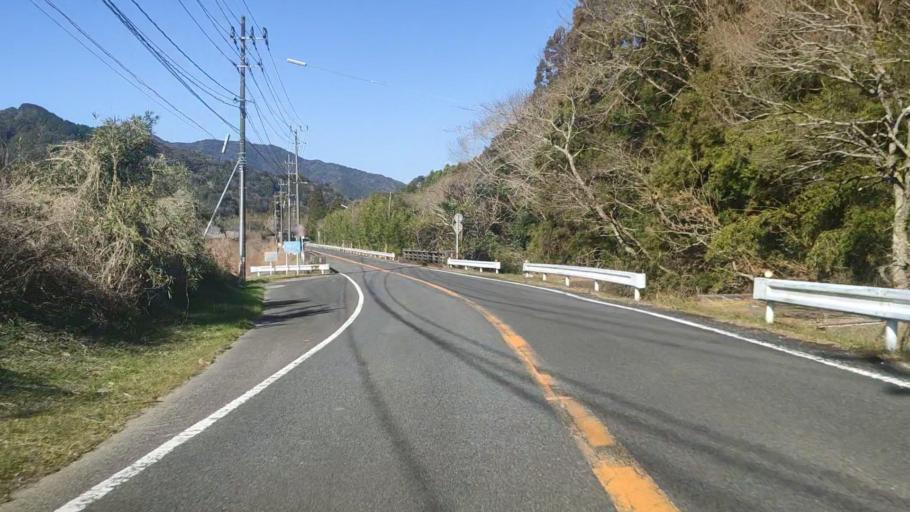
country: JP
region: Oita
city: Saiki
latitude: 32.8994
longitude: 131.9357
